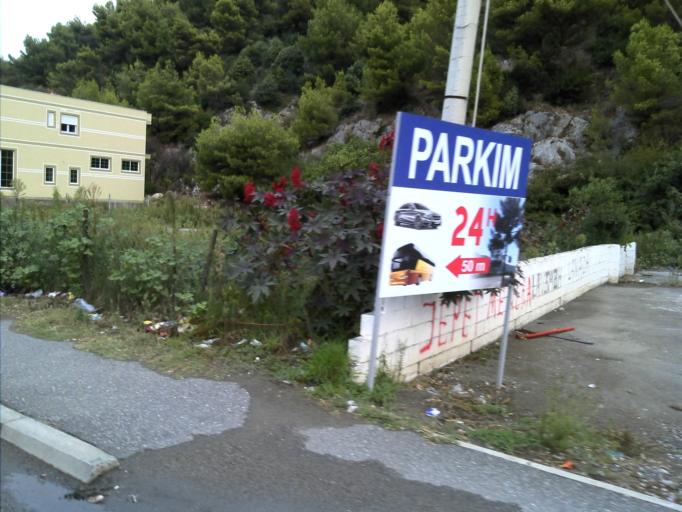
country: AL
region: Lezhe
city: Shengjin
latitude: 41.8089
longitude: 19.6025
